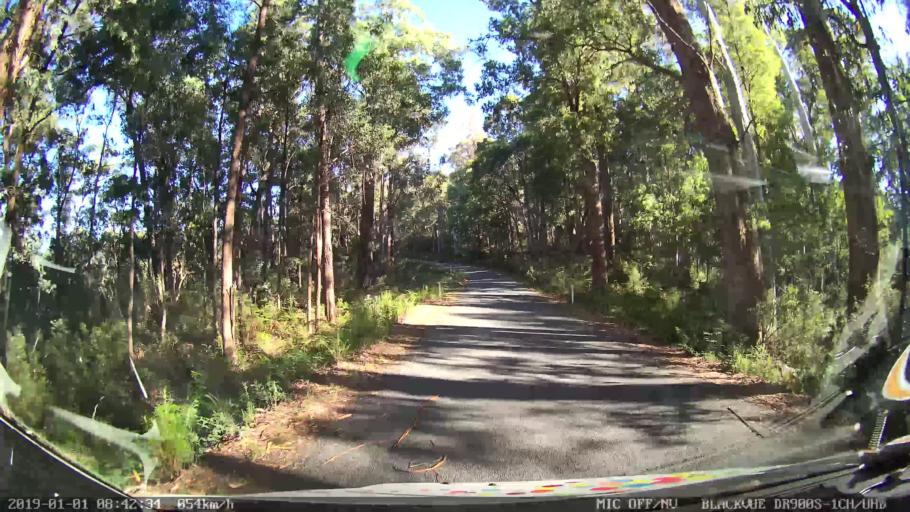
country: AU
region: New South Wales
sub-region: Snowy River
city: Jindabyne
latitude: -36.3229
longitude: 148.1928
